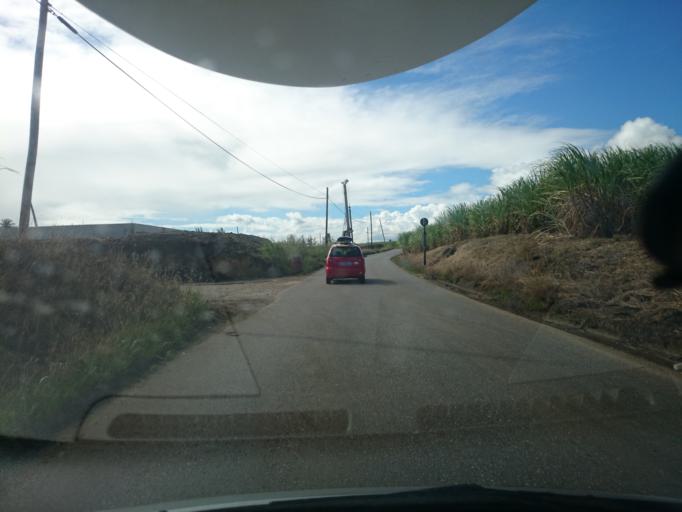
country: BB
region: Christ Church
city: Oistins
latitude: 13.1098
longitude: -59.5323
